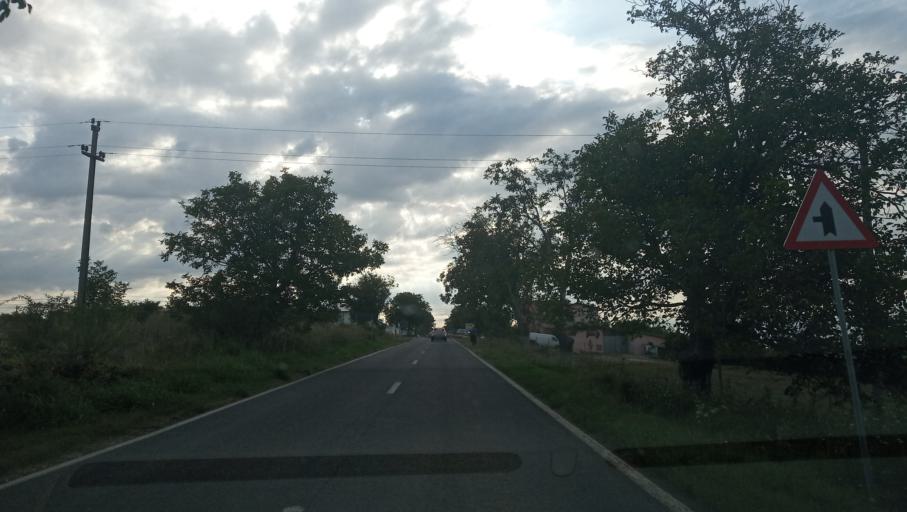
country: RO
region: Constanta
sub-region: Comuna Ostrov
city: Ostrov
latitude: 44.1023
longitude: 27.3788
